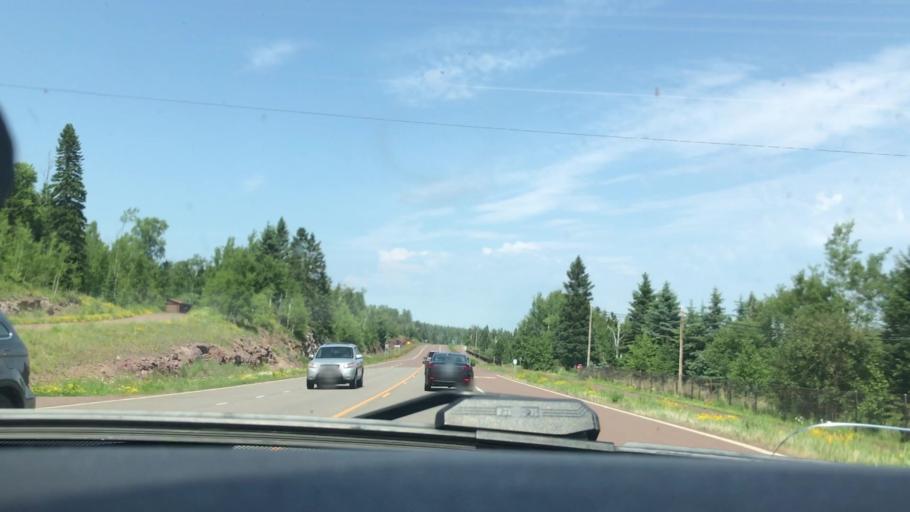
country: US
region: Minnesota
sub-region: Cook County
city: Grand Marais
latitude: 47.6000
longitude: -90.7878
